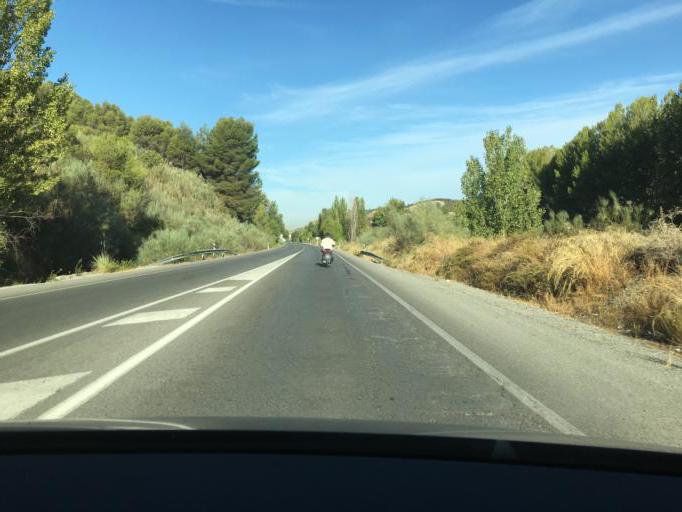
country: ES
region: Andalusia
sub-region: Provincia de Granada
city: Cenes de la Vega
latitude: 37.1573
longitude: -3.5488
